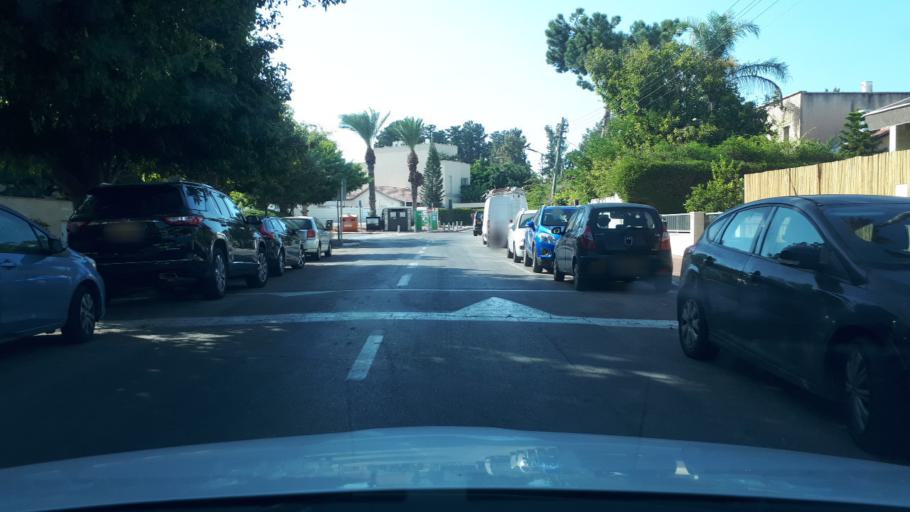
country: IL
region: Tel Aviv
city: Giv`atayim
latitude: 32.0580
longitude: 34.8271
